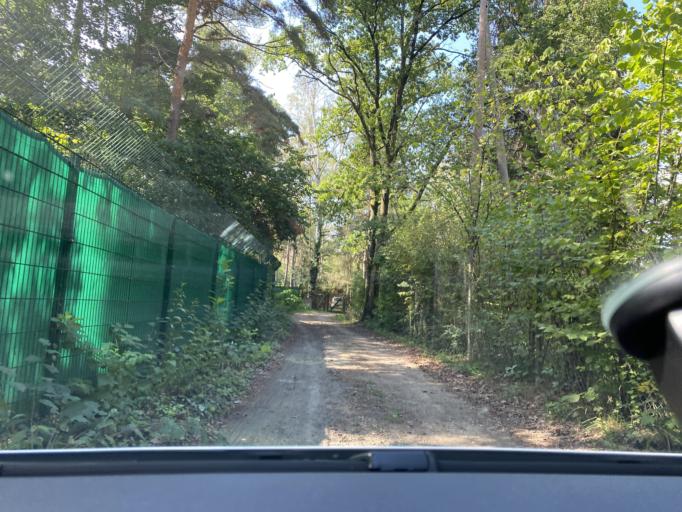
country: DE
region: Bavaria
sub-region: Regierungsbezirk Mittelfranken
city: Furth
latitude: 49.5009
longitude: 10.9904
